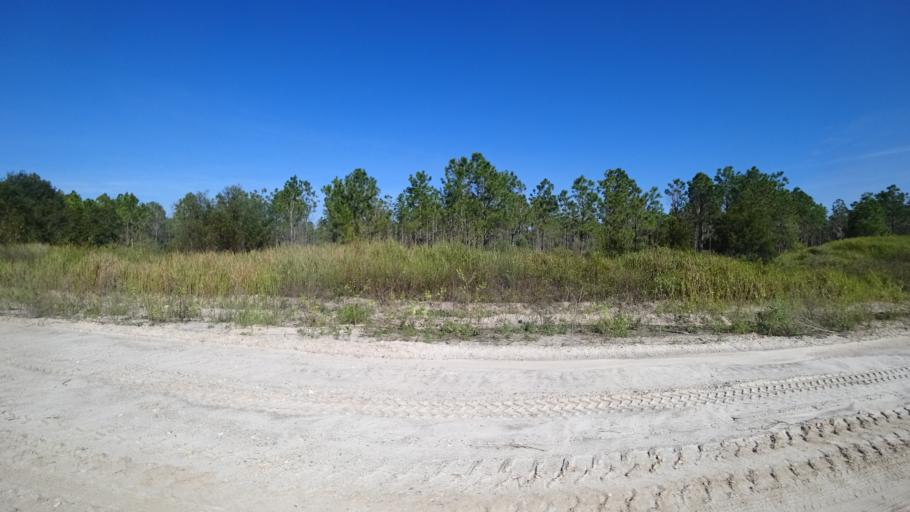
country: US
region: Florida
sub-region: Hillsborough County
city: Balm
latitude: 27.6485
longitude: -82.1018
